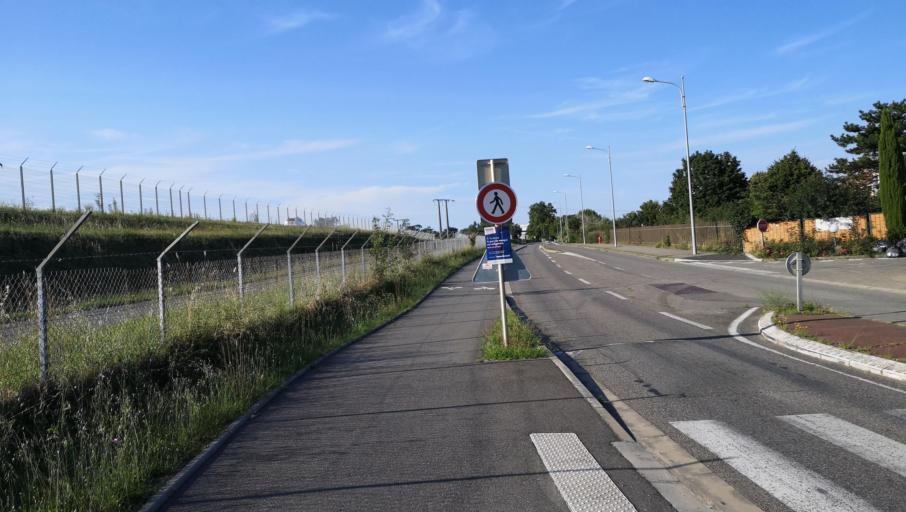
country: FR
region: Midi-Pyrenees
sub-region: Departement de la Haute-Garonne
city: Blagnac
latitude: 43.6157
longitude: 1.3875
